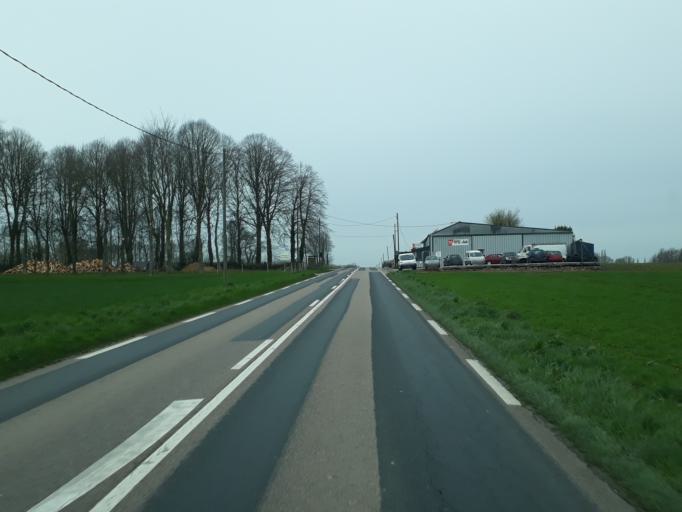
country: FR
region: Haute-Normandie
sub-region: Departement de la Seine-Maritime
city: Breaute
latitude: 49.6110
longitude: 0.4108
